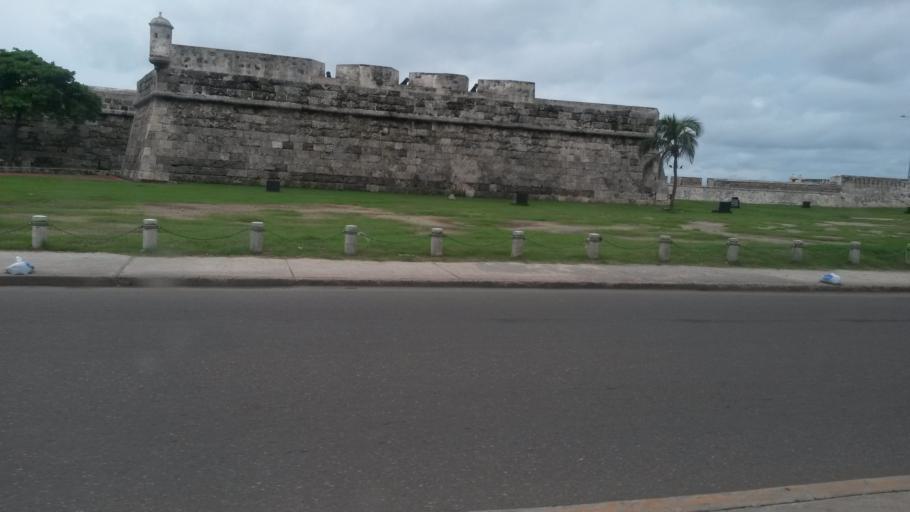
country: CO
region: Bolivar
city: Cartagena
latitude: 10.4310
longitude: -75.5450
